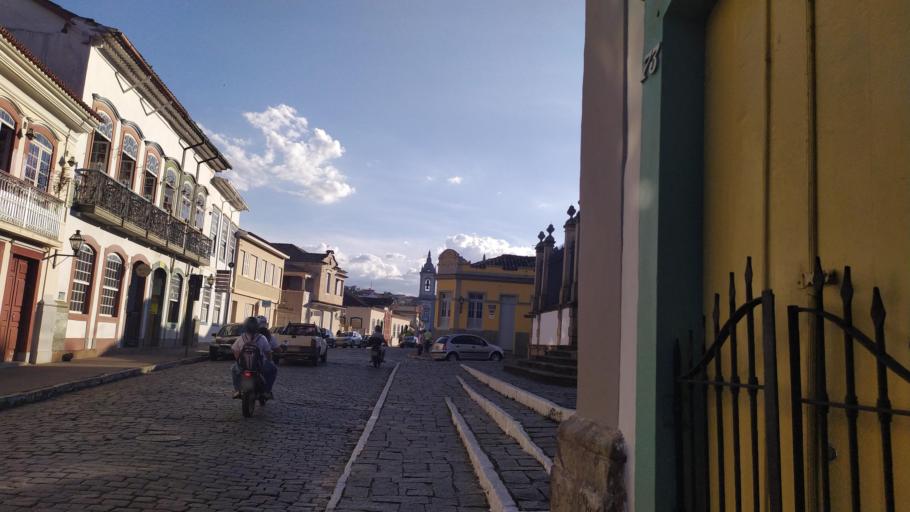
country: BR
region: Minas Gerais
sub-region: Sao Joao Del Rei
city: Sao Joao del Rei
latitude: -21.1351
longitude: -44.2617
